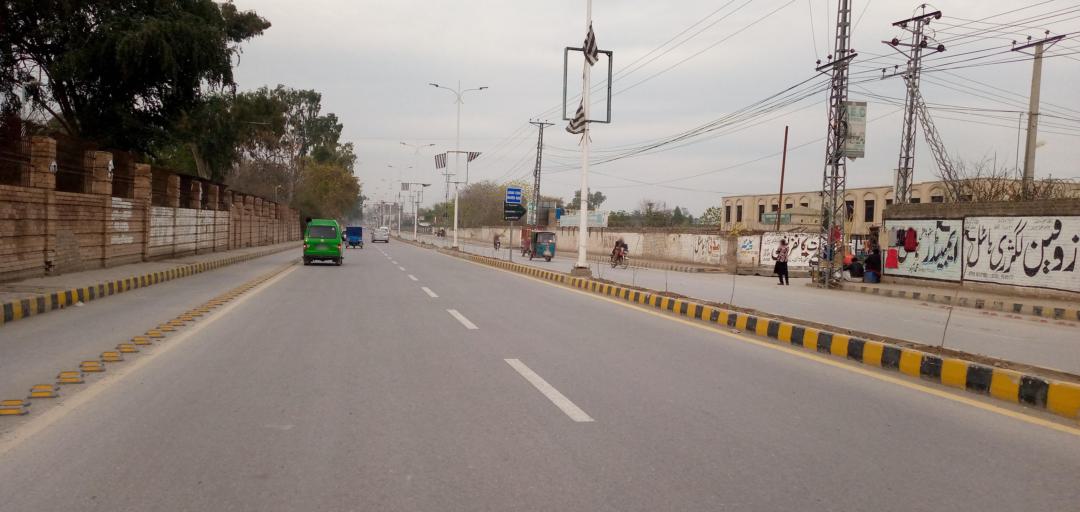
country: PK
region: Khyber Pakhtunkhwa
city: Peshawar
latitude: 34.0126
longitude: 71.4891
